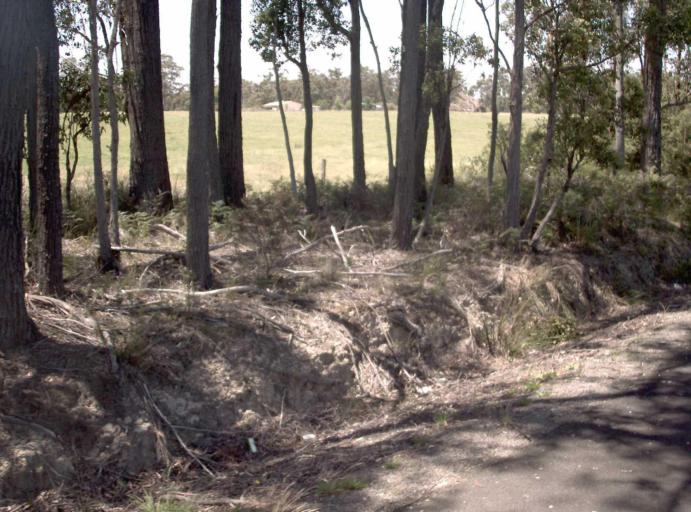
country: AU
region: Victoria
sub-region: East Gippsland
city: Lakes Entrance
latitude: -37.7382
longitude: 148.1517
